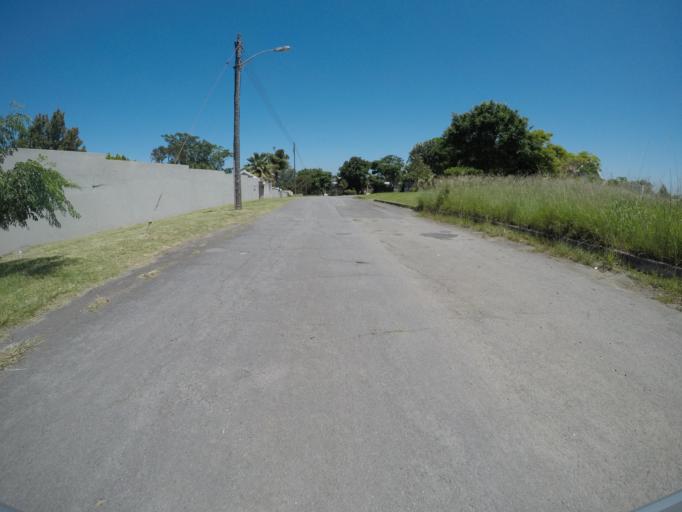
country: ZA
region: Eastern Cape
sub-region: Buffalo City Metropolitan Municipality
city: East London
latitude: -32.9589
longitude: 27.9394
